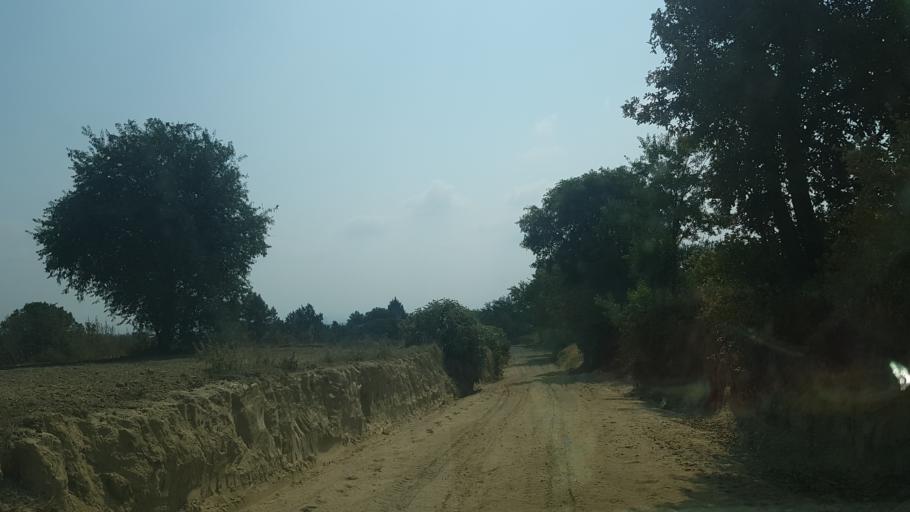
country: MX
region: Puebla
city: Domingo Arenas
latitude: 19.1295
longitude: -98.5070
